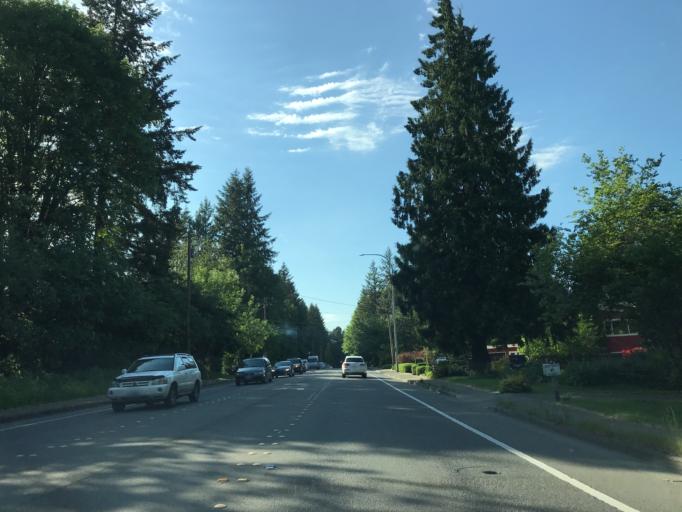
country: US
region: Washington
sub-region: King County
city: Issaquah
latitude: 47.5200
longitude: -122.0316
